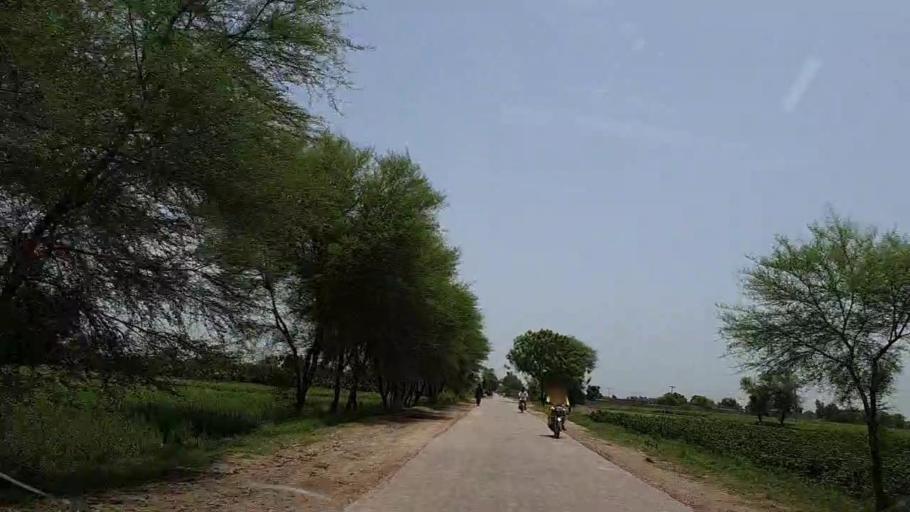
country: PK
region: Sindh
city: Tharu Shah
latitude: 26.9596
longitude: 68.0662
